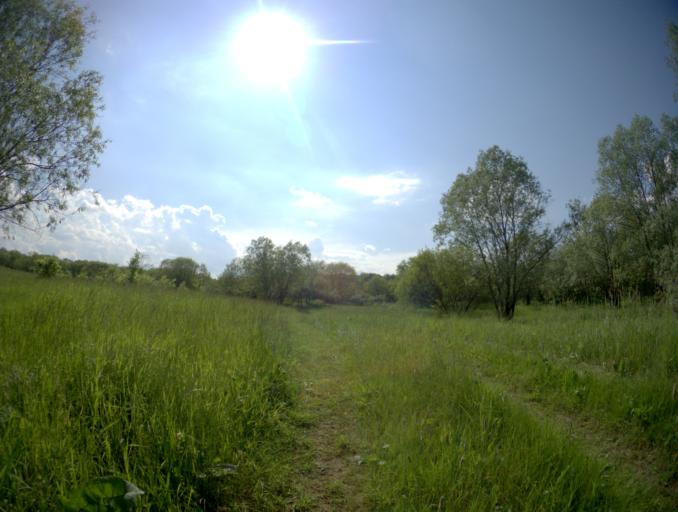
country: RU
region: Vladimir
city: Raduzhnyy
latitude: 56.0480
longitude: 40.2940
